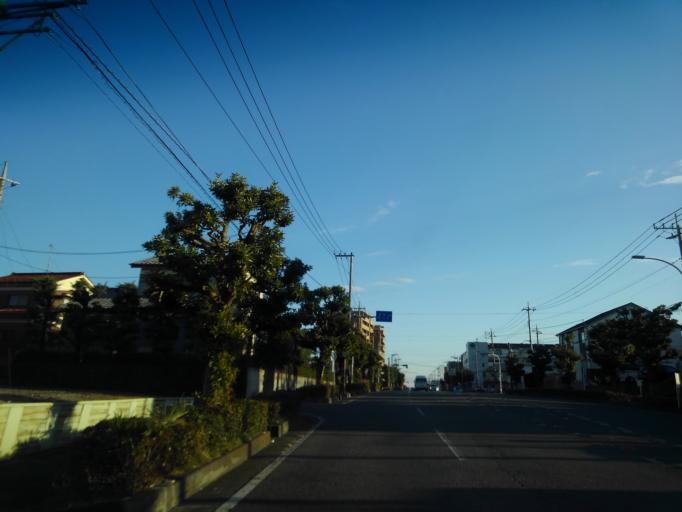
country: JP
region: Saitama
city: Tokorozawa
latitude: 35.7944
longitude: 139.5044
